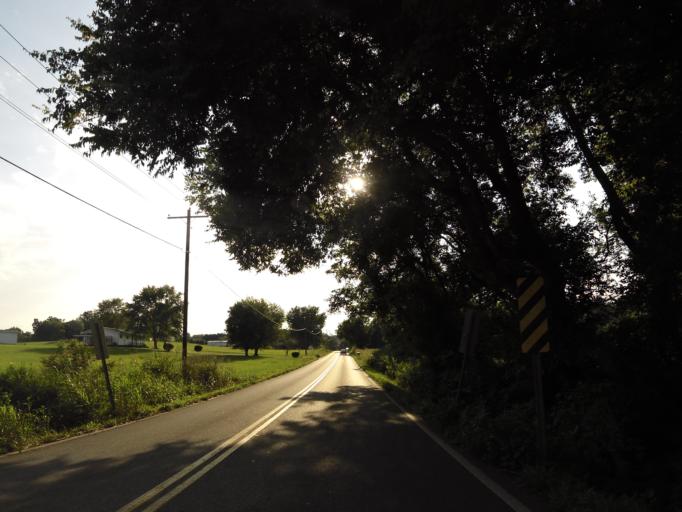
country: US
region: Tennessee
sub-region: Monroe County
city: Sweetwater
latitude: 35.6019
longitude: -84.3866
